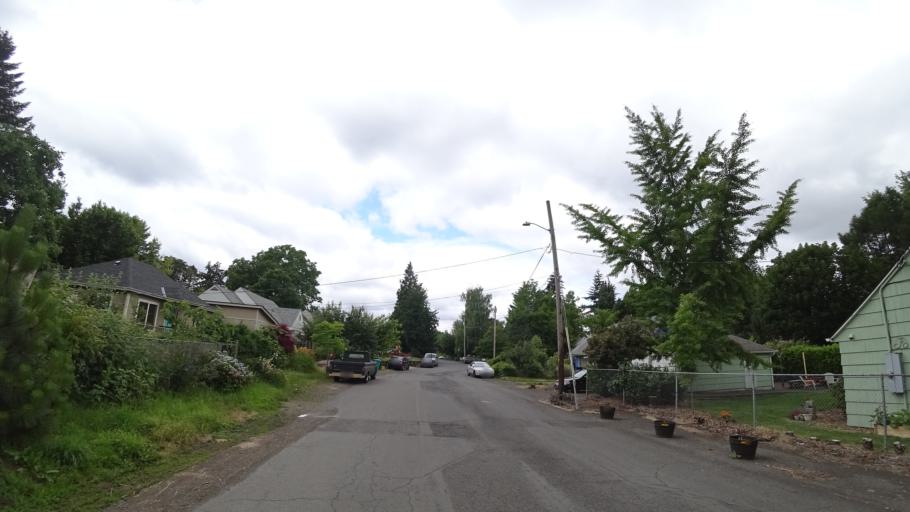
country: US
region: Oregon
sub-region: Multnomah County
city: Lents
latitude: 45.5604
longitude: -122.5891
